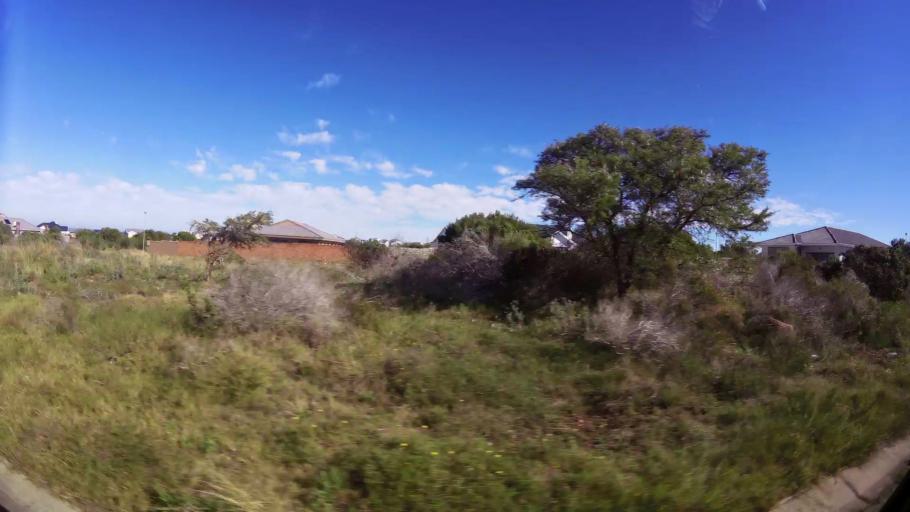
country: ZA
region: Eastern Cape
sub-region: Cacadu District Municipality
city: Jeffrey's Bay
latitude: -34.0353
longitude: 24.9083
